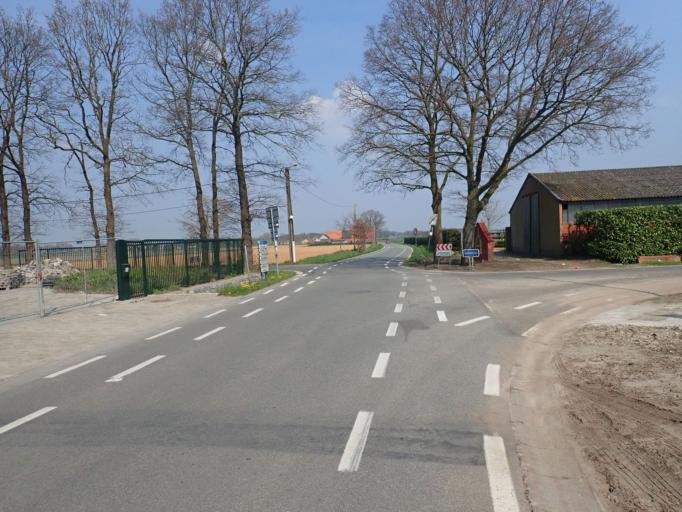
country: BE
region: Flanders
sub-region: Provincie Antwerpen
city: Essen
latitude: 51.4519
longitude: 4.4992
